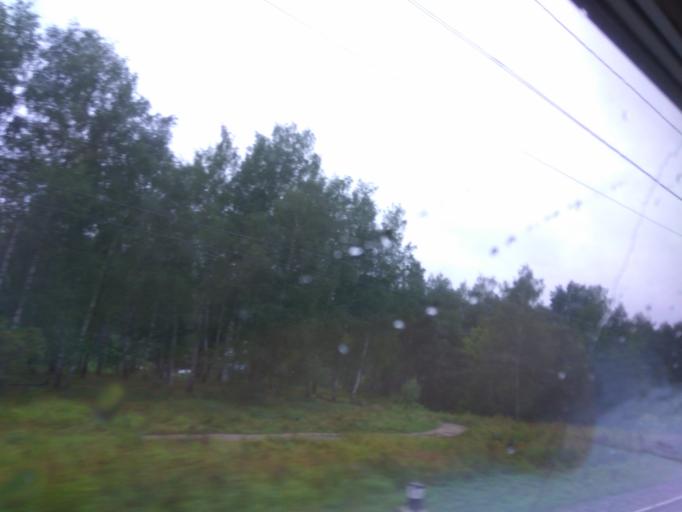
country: RU
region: Moskovskaya
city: Stupino
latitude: 54.8793
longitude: 38.1086
